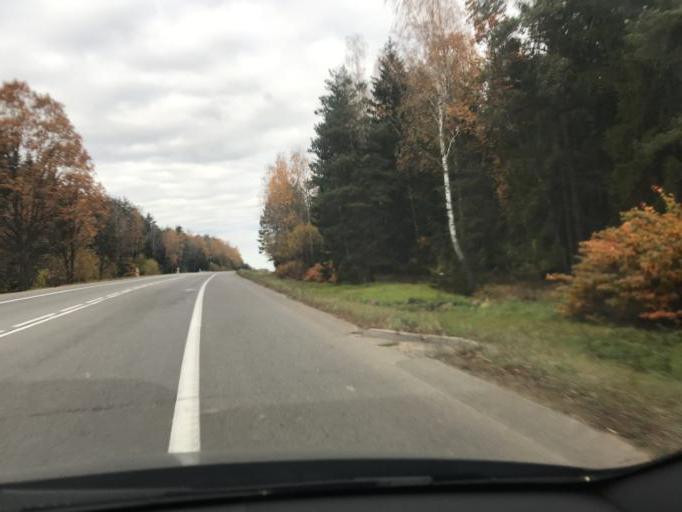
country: BY
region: Minsk
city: Korolev Stan
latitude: 54.0368
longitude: 27.8199
